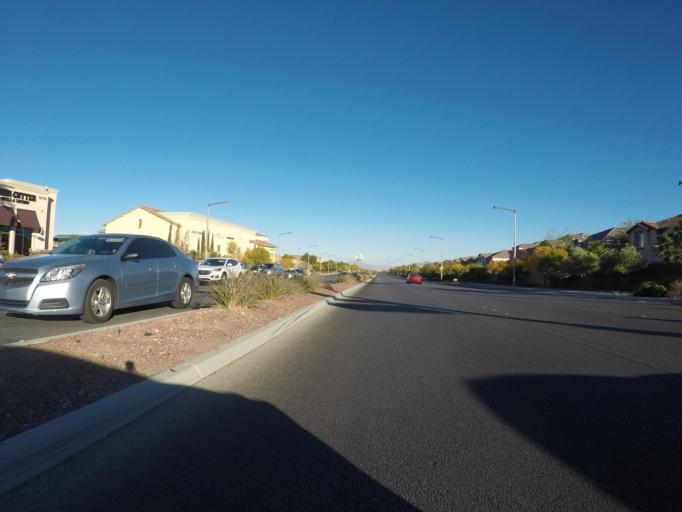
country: US
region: Nevada
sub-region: Clark County
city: Summerlin South
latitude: 36.1589
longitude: -115.3517
